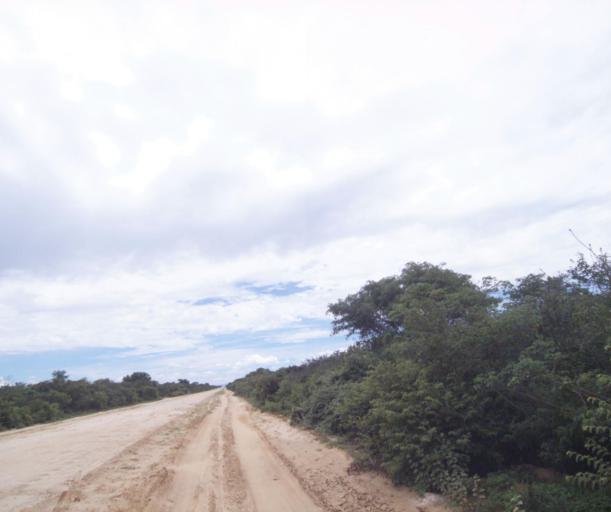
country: BR
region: Bahia
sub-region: Carinhanha
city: Carinhanha
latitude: -14.2480
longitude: -43.8403
